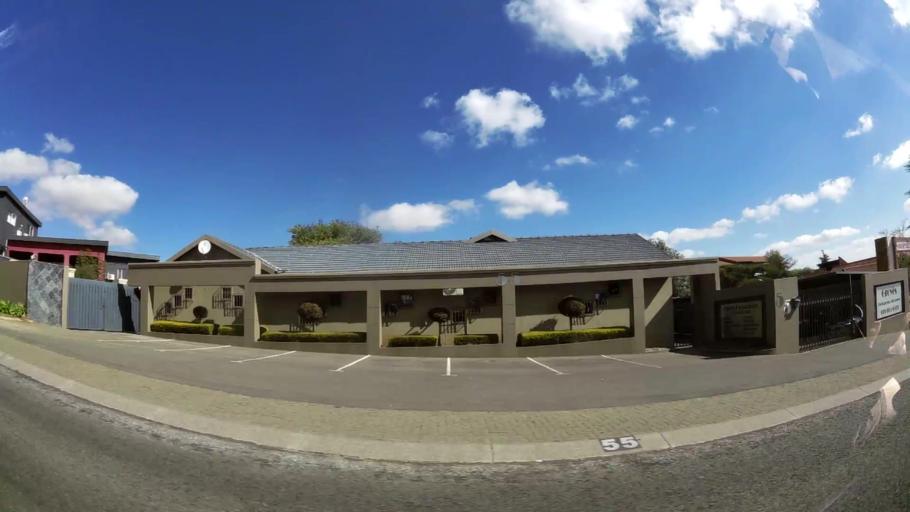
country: ZA
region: Gauteng
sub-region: West Rand District Municipality
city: Krugersdorp
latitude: -26.0995
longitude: 27.8041
